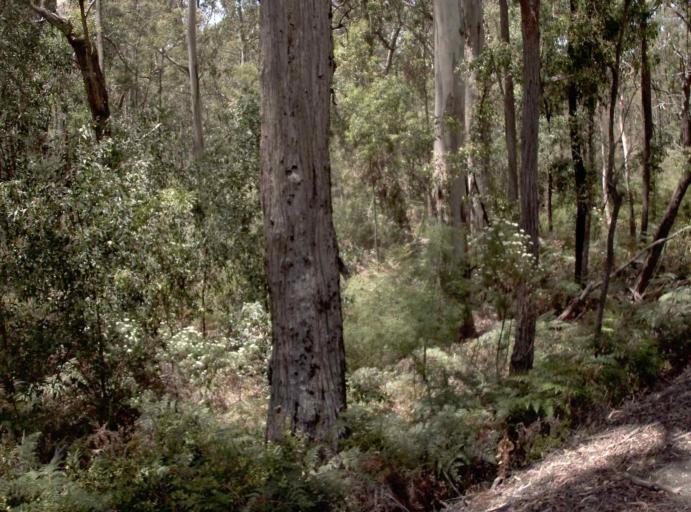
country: AU
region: Victoria
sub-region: East Gippsland
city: Lakes Entrance
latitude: -37.6330
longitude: 147.8948
